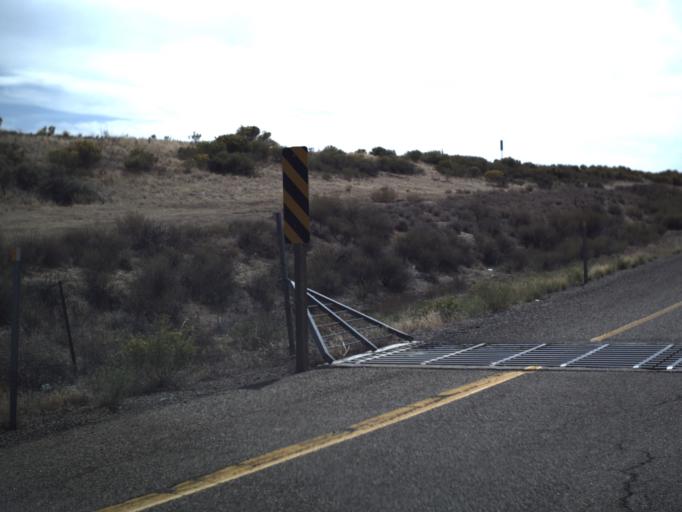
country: US
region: Colorado
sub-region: Mesa County
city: Loma
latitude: 39.1746
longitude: -109.1285
